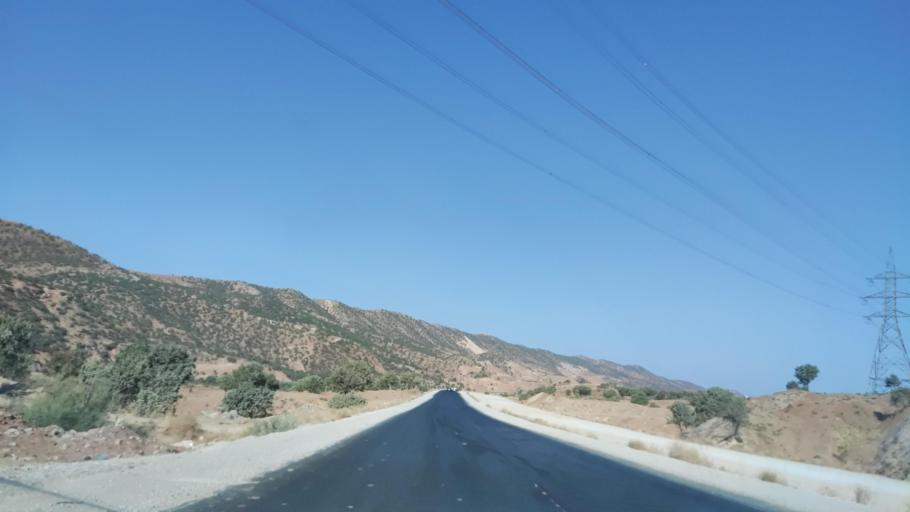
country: IQ
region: Arbil
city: Shaqlawah
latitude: 36.4299
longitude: 44.3297
